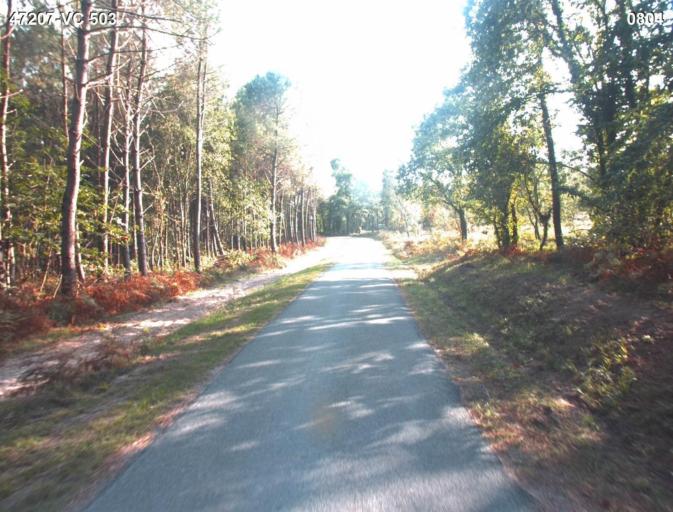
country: FR
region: Aquitaine
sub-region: Departement du Lot-et-Garonne
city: Barbaste
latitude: 44.1996
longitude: 0.2322
